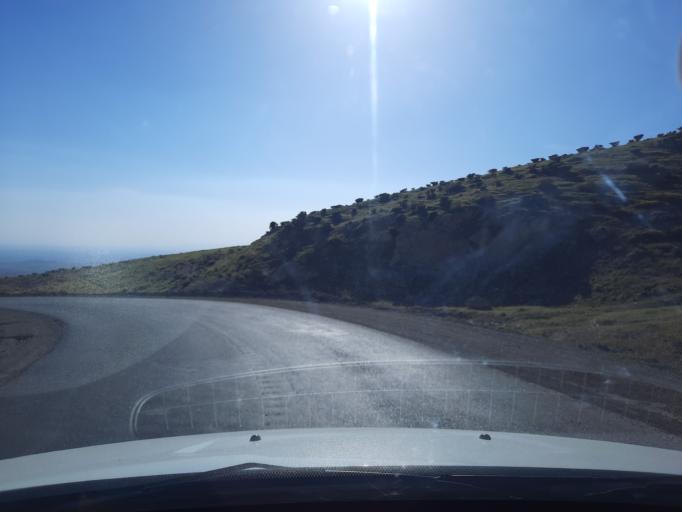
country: IR
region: Qazvin
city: Qazvin
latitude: 36.3681
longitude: 50.2011
